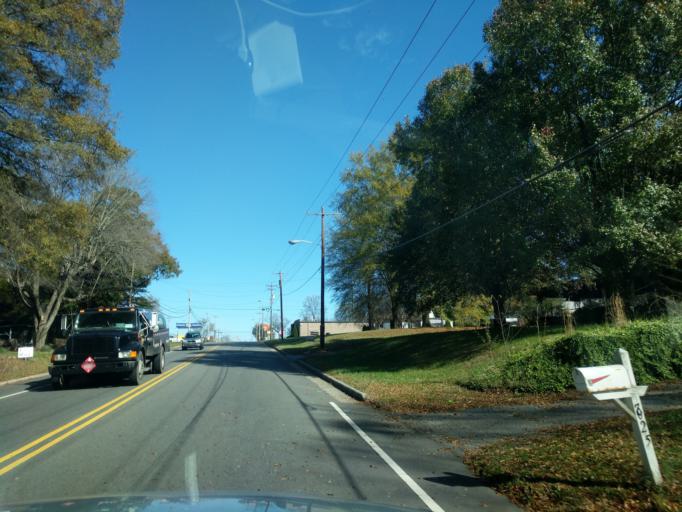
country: US
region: North Carolina
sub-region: Iredell County
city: Statesville
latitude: 35.7814
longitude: -80.9224
